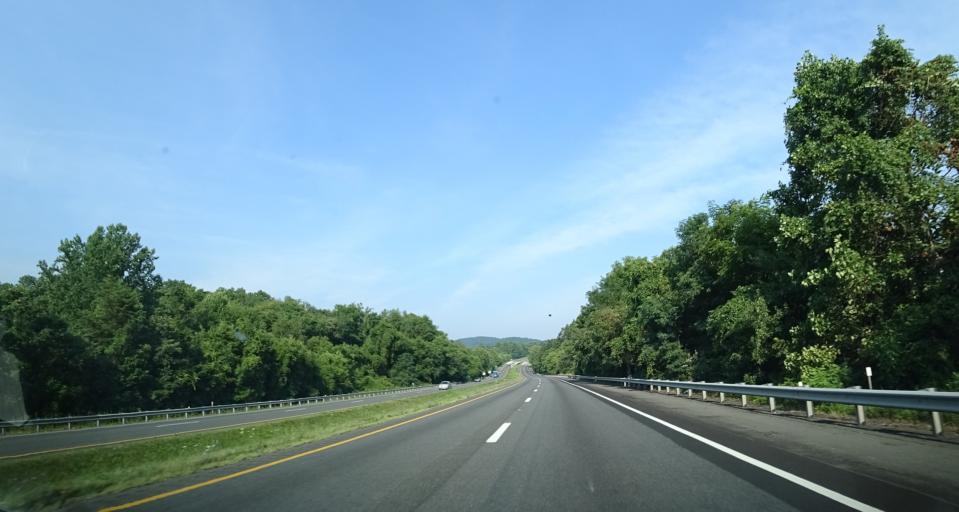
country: US
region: Virginia
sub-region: Fauquier County
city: Marshall
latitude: 38.9023
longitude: -77.9319
